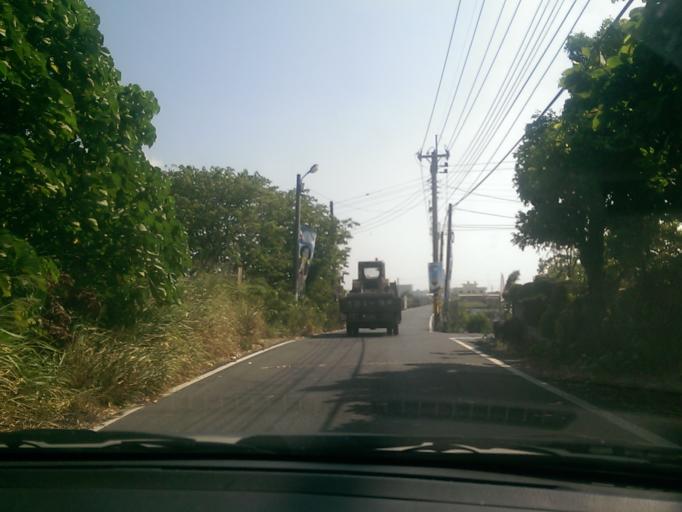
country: TW
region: Taiwan
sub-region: Changhua
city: Chang-hua
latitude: 23.9662
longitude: 120.5109
